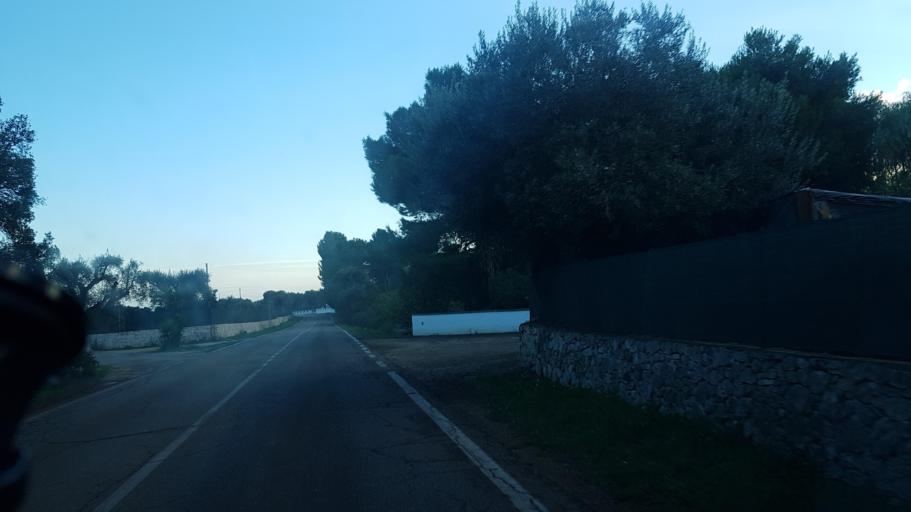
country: IT
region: Apulia
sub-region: Provincia di Brindisi
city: Ostuni
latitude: 40.6949
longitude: 17.5960
